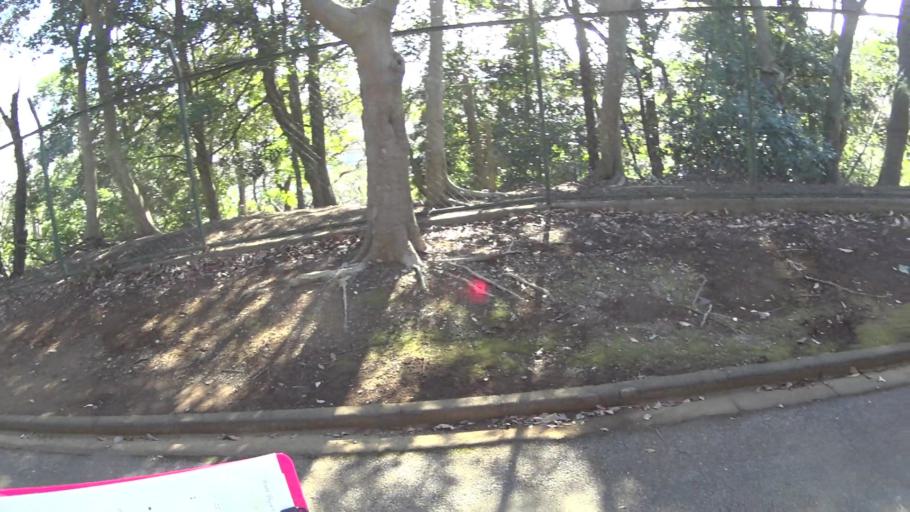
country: JP
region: Chiba
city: Chiba
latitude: 35.6436
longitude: 140.1256
